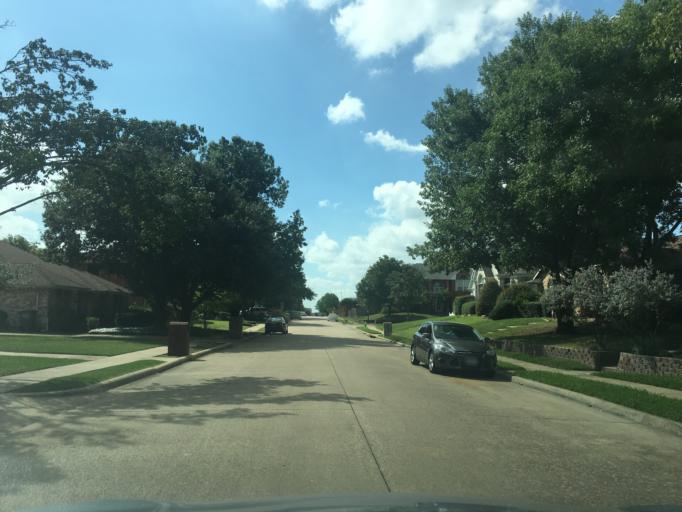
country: US
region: Texas
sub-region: Dallas County
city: Sachse
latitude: 32.9695
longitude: -96.5946
